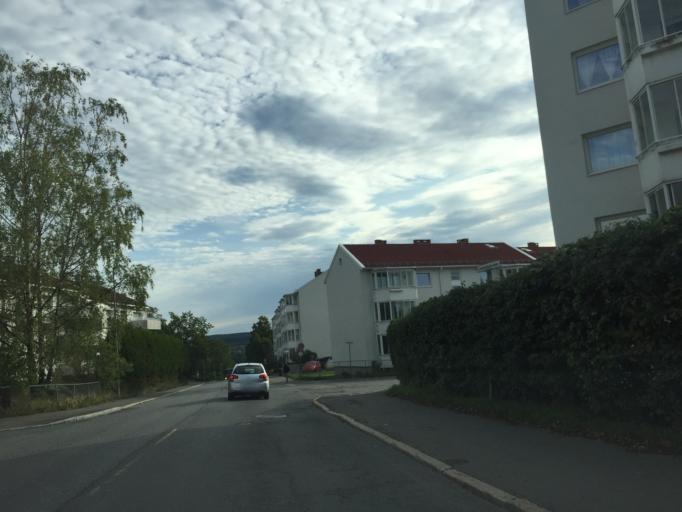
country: NO
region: Akershus
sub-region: Oppegard
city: Kolbotn
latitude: 59.8748
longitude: 10.8149
